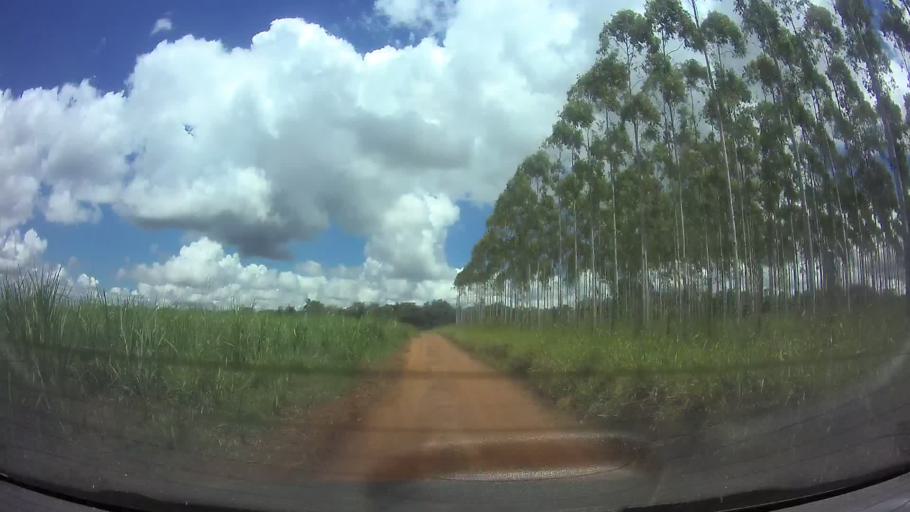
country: PY
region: Paraguari
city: La Colmena
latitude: -25.9665
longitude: -56.7337
